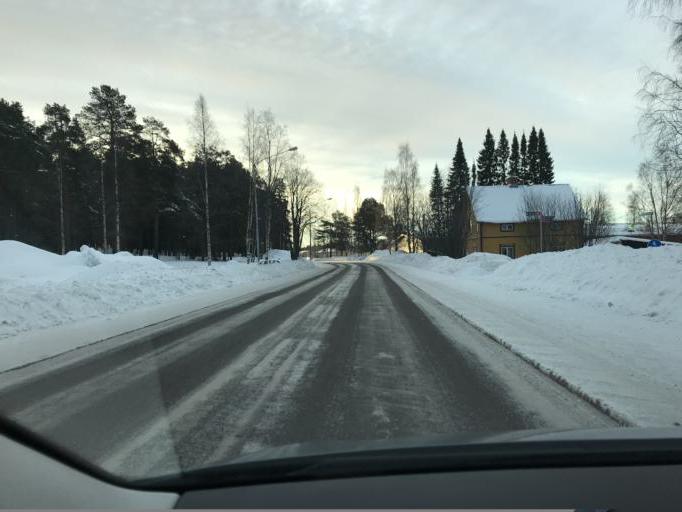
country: SE
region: Norrbotten
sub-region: Lulea Kommun
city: Bergnaset
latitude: 65.6107
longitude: 22.1001
